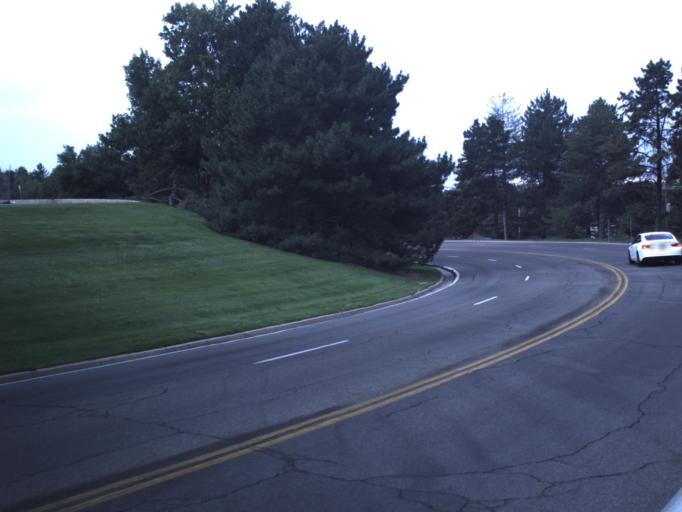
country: US
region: Utah
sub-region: Salt Lake County
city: Salt Lake City
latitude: 40.7710
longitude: -111.8472
